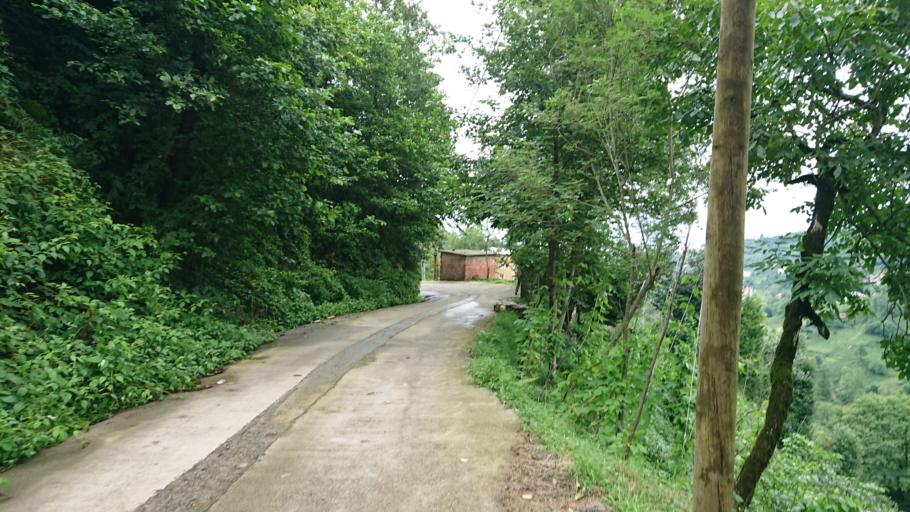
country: TR
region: Rize
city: Rize
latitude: 40.9760
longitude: 40.4858
